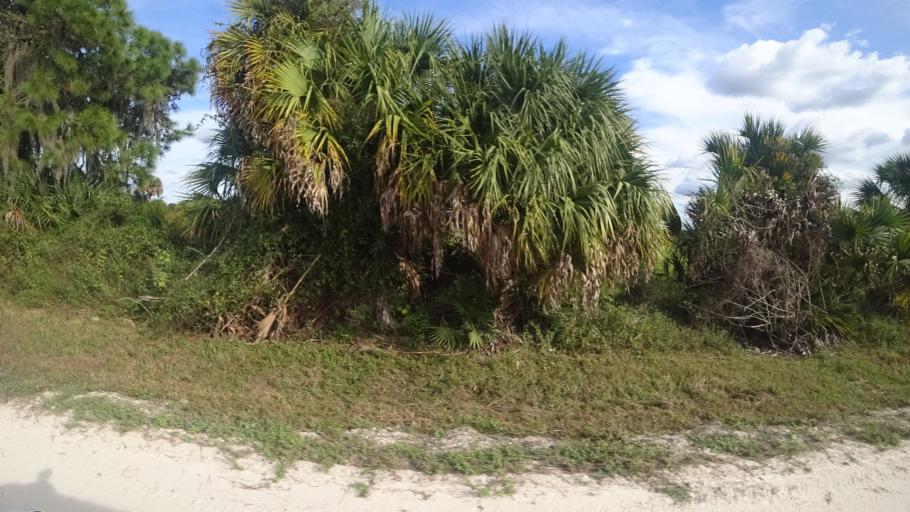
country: US
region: Florida
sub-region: Sarasota County
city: Warm Mineral Springs
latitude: 27.2511
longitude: -82.1637
